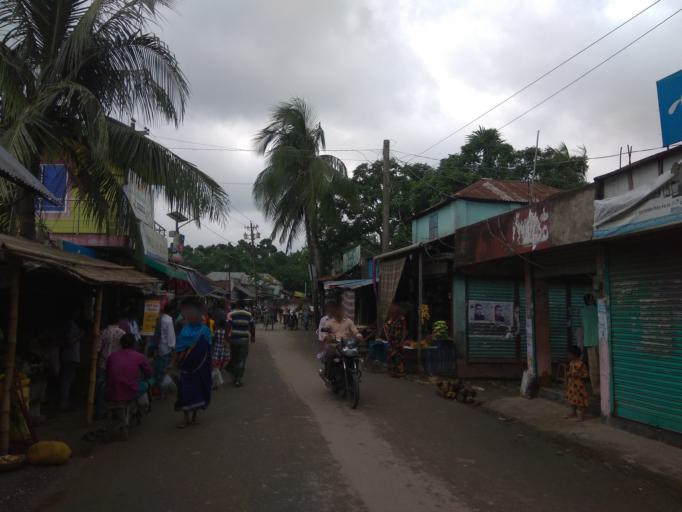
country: BD
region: Dhaka
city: Dohar
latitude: 23.4389
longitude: 90.0734
